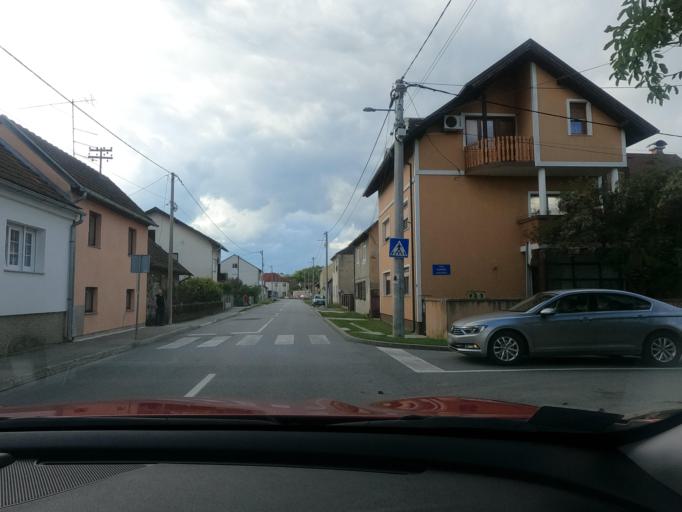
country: HR
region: Sisacko-Moslavacka
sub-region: Grad Sisak
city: Sisak
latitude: 45.4860
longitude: 16.3833
